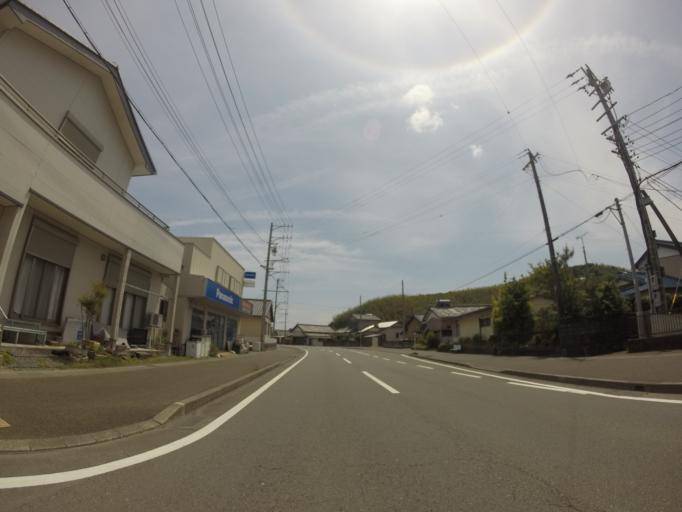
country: JP
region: Shizuoka
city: Fujieda
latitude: 34.8944
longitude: 138.2490
